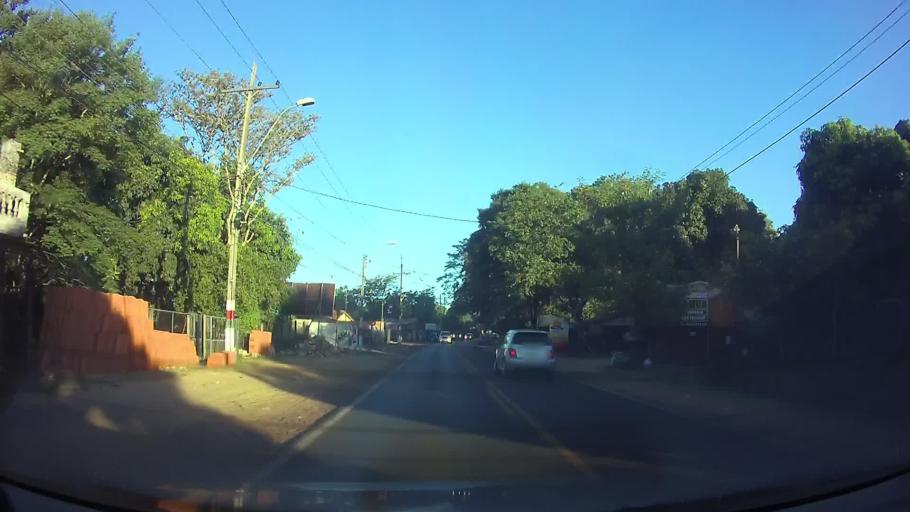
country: PY
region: Central
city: Aregua
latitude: -25.2988
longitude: -57.4115
